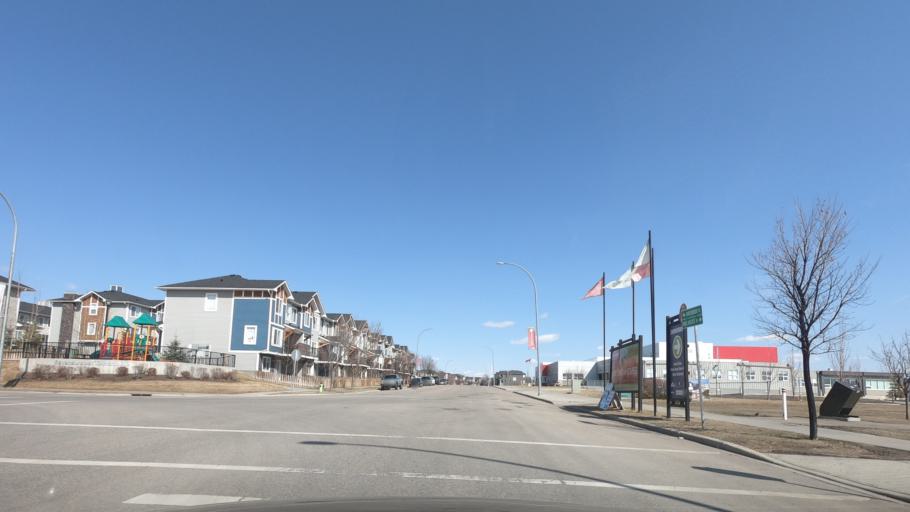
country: CA
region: Alberta
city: Airdrie
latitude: 51.2671
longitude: -113.9819
